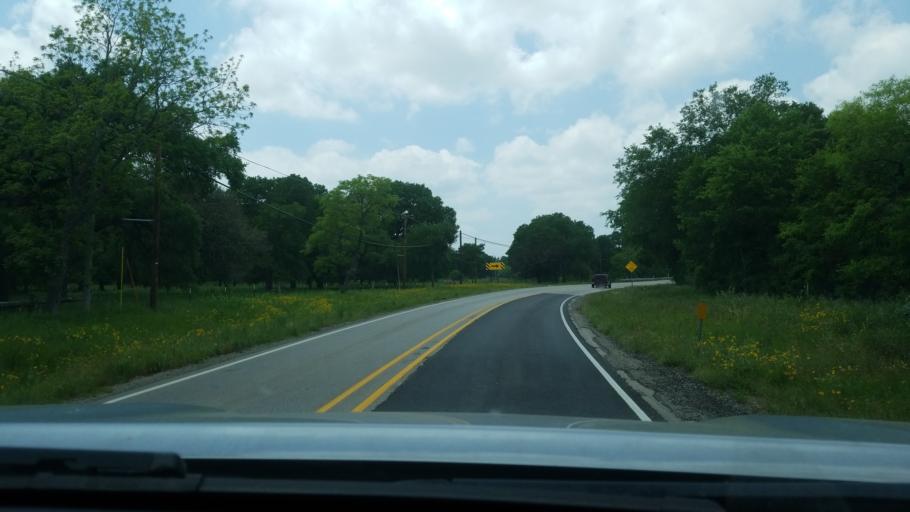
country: US
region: Texas
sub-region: Hays County
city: Dripping Springs
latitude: 30.1438
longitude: -98.0461
